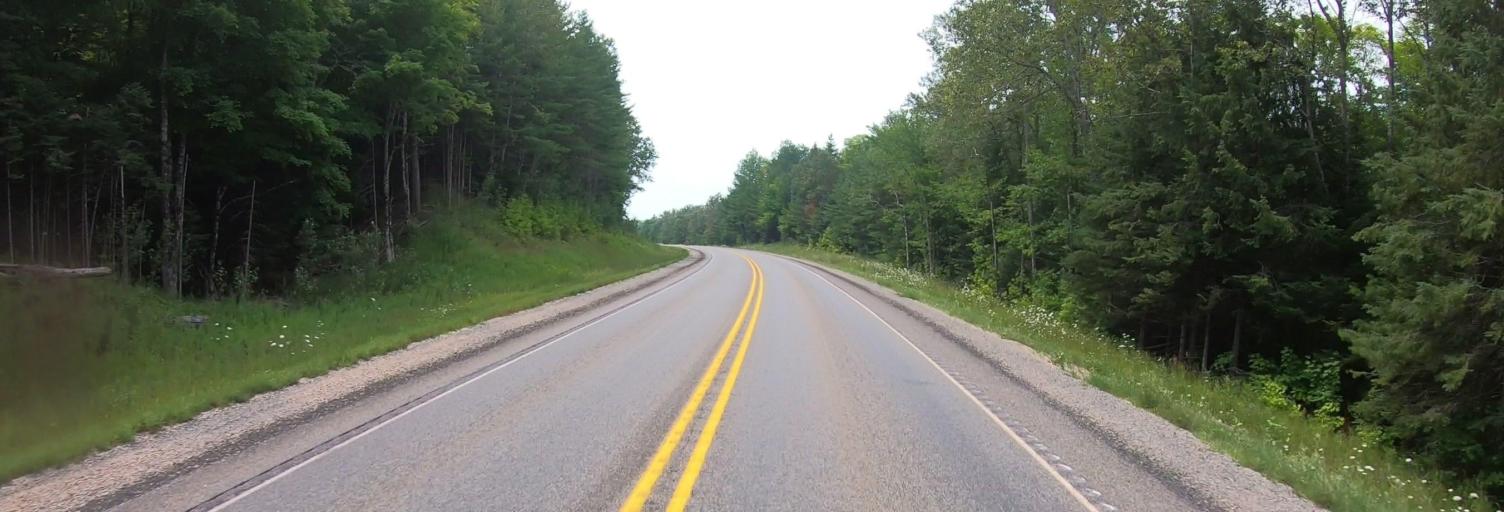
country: US
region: Michigan
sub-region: Alger County
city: Munising
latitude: 46.3337
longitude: -86.8331
